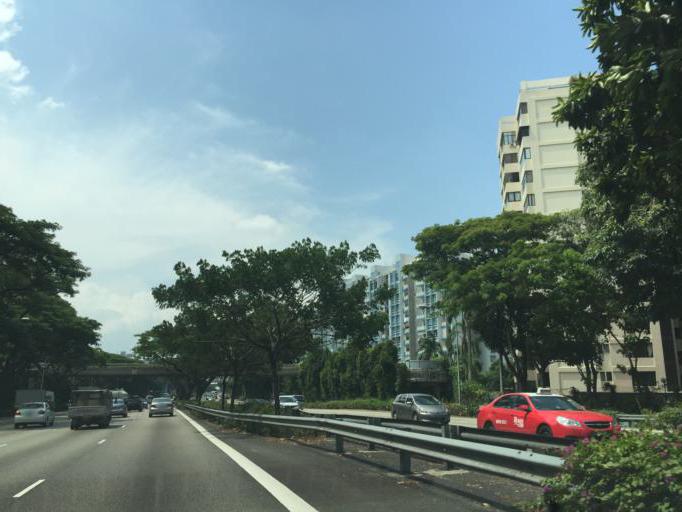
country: SG
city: Singapore
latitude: 1.3277
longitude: 103.9098
